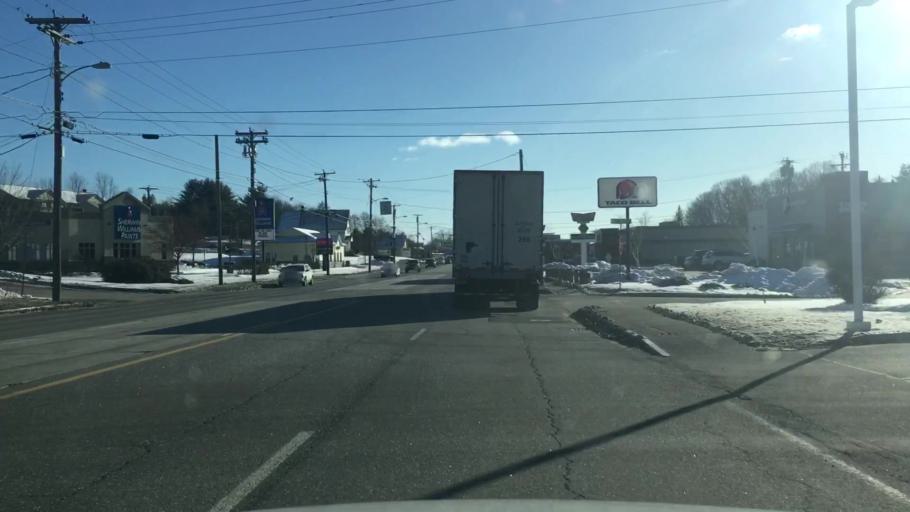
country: US
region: Maine
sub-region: Androscoggin County
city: Lewiston
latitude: 44.1184
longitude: -70.2252
